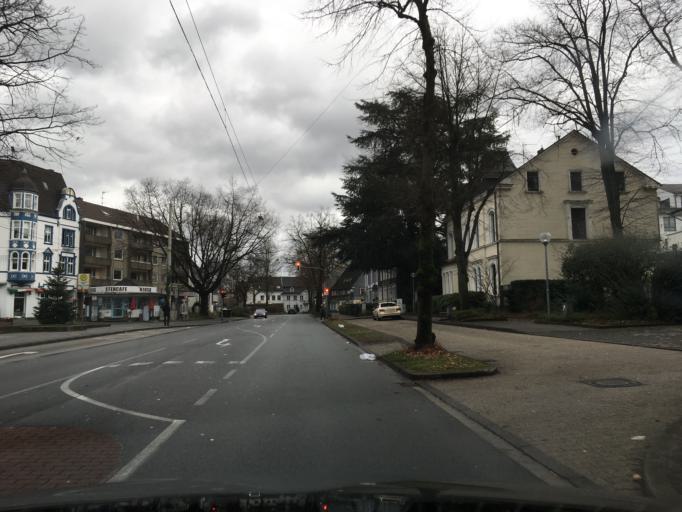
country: DE
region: North Rhine-Westphalia
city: Haan
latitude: 51.1928
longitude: 7.0124
